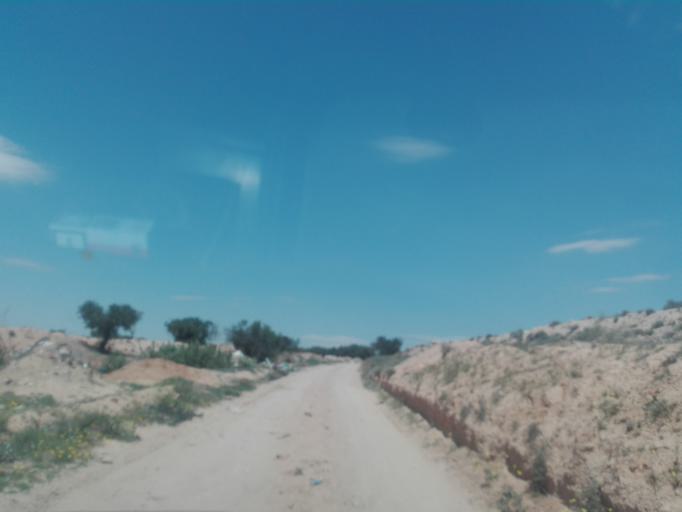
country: TN
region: Safaqis
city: Sfax
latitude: 34.6784
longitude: 10.6122
